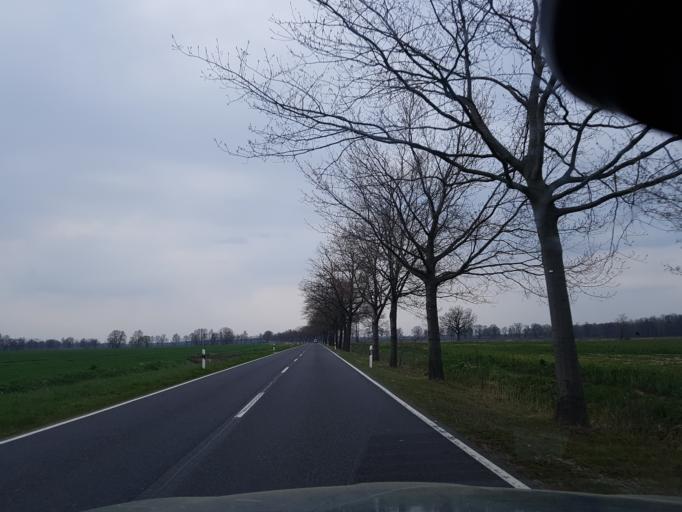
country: DE
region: Brandenburg
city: Grosskmehlen
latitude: 51.3938
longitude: 13.7075
